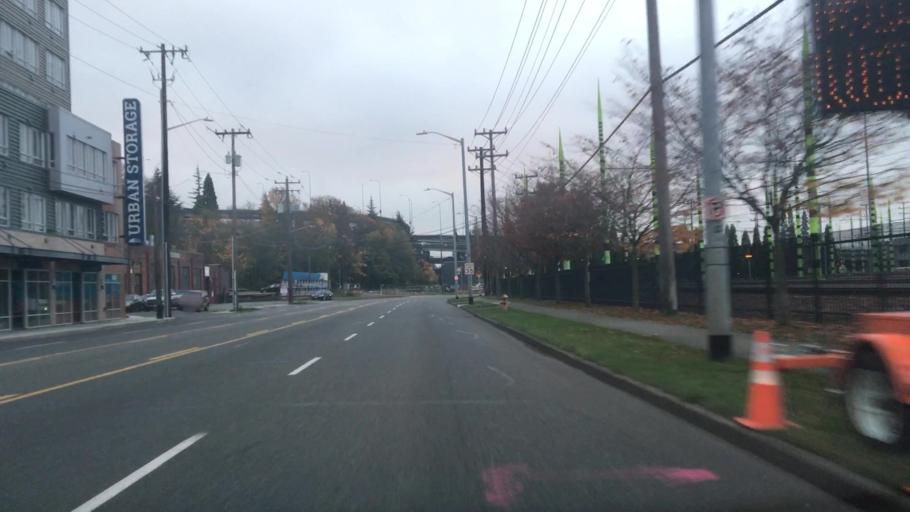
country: US
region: Washington
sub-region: King County
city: Seattle
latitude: 47.5748
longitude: -122.3215
